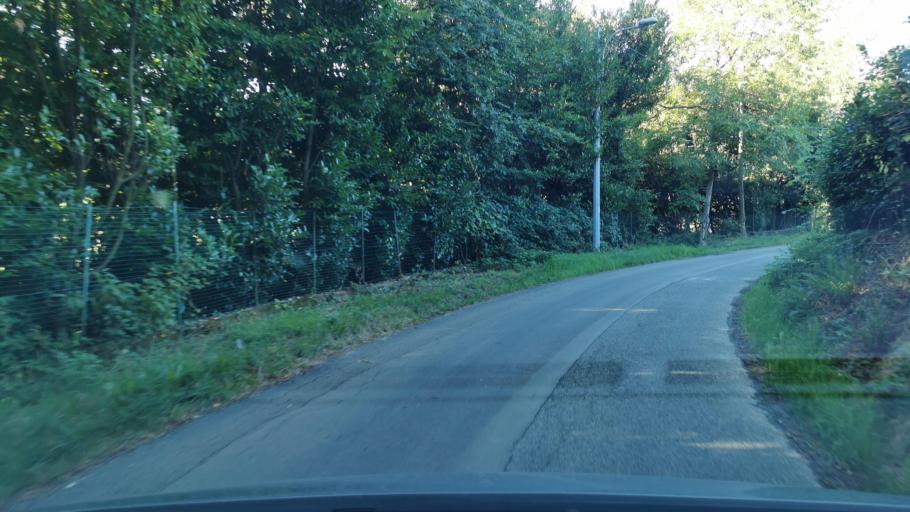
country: IT
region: Piedmont
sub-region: Provincia di Torino
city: Corio
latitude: 45.3086
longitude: 7.5248
